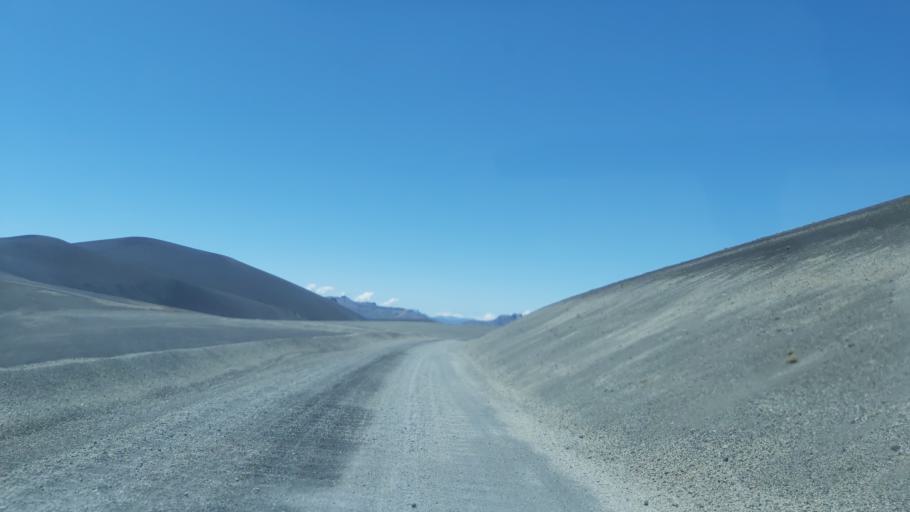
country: CL
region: Araucania
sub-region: Provincia de Cautin
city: Vilcun
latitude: -38.3784
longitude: -71.5452
